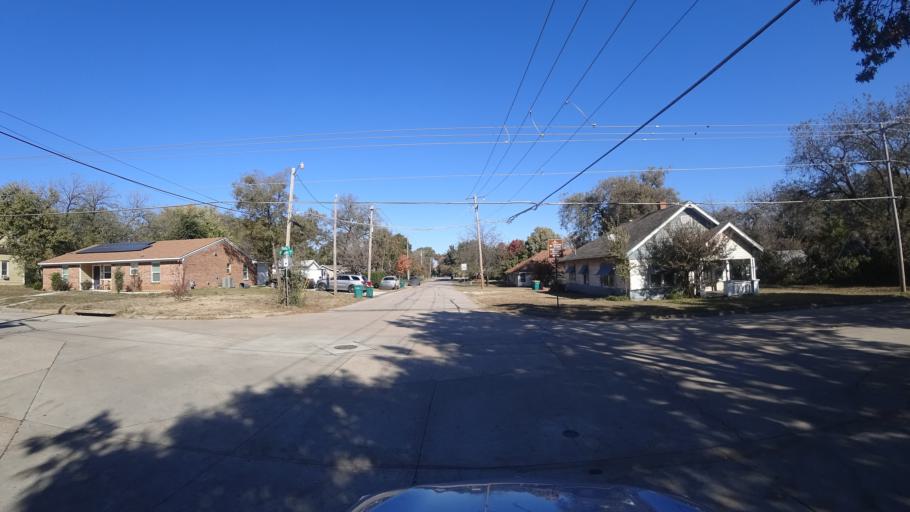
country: US
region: Texas
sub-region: Denton County
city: Lewisville
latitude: 33.0492
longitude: -96.9965
